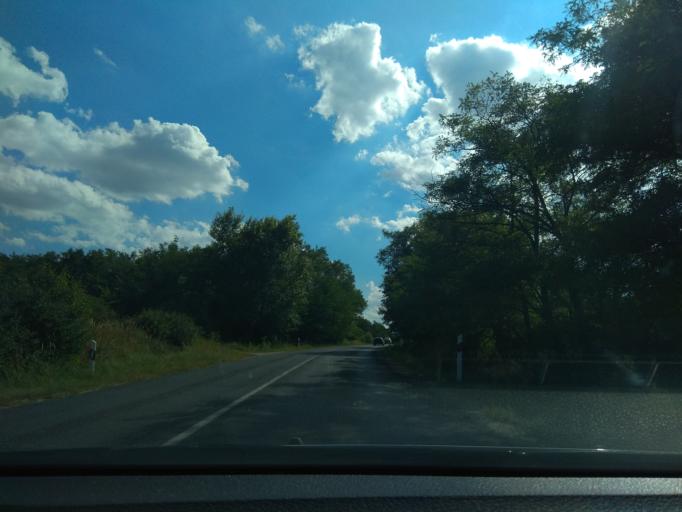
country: HU
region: Borsod-Abauj-Zemplen
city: Malyi
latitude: 48.0470
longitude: 20.7930
